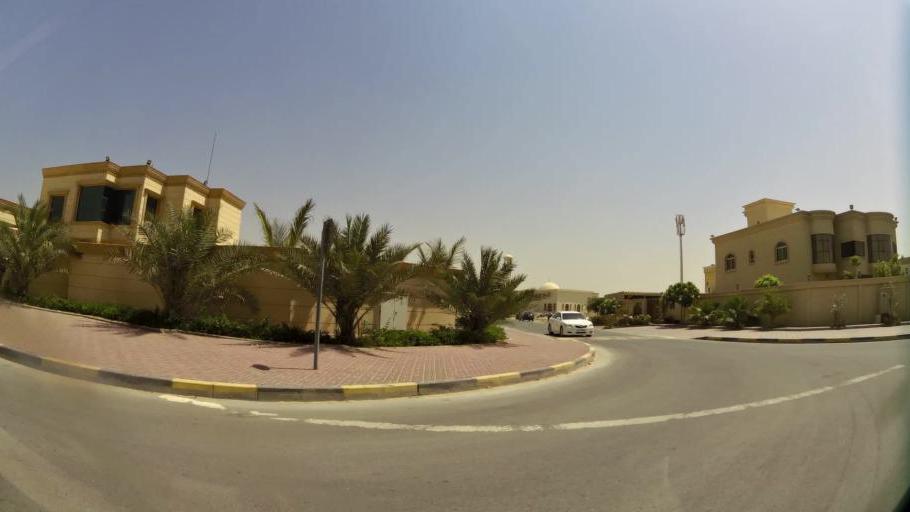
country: AE
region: Ajman
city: Ajman
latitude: 25.4140
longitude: 55.5145
